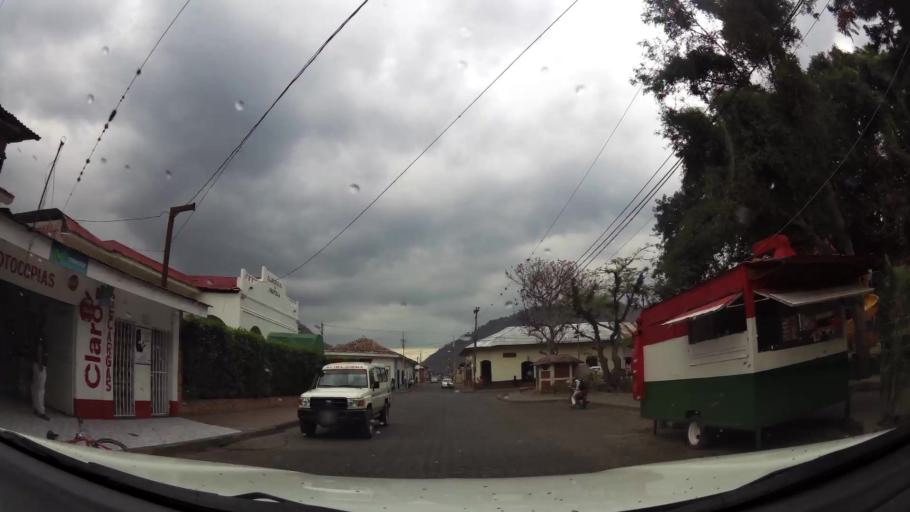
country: NI
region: Jinotega
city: Jinotega
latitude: 13.0921
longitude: -86.0037
